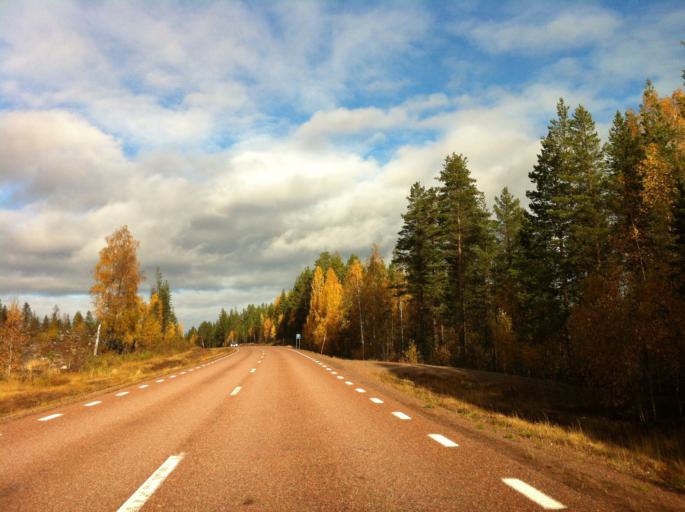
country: SE
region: Dalarna
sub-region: Alvdalens Kommun
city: AElvdalen
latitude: 61.5068
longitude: 13.3881
